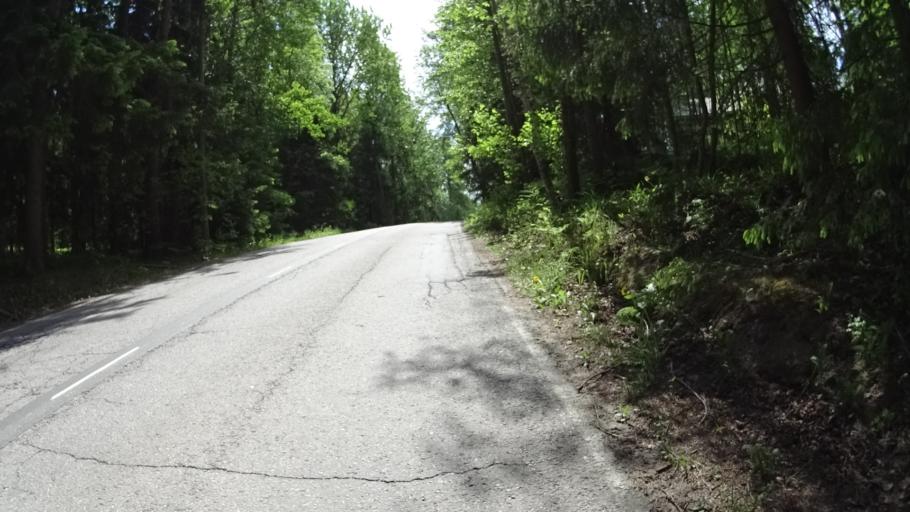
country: FI
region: Uusimaa
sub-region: Helsinki
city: Espoo
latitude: 60.2538
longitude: 24.6528
